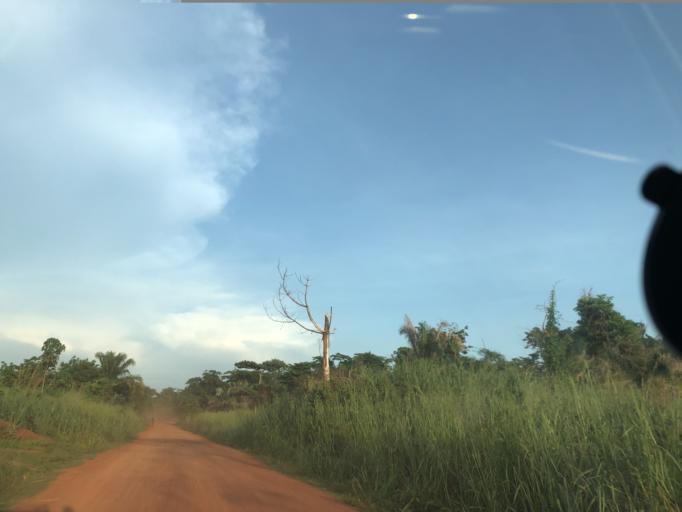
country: CF
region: Bangui
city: Bangui
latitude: 4.2263
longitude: 18.6707
